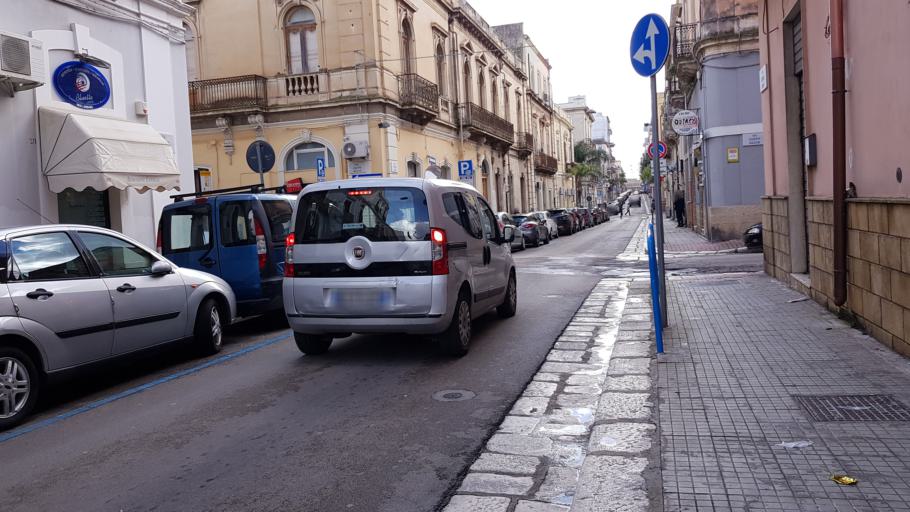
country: IT
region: Apulia
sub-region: Provincia di Brindisi
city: Brindisi
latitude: 40.6360
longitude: 17.9409
